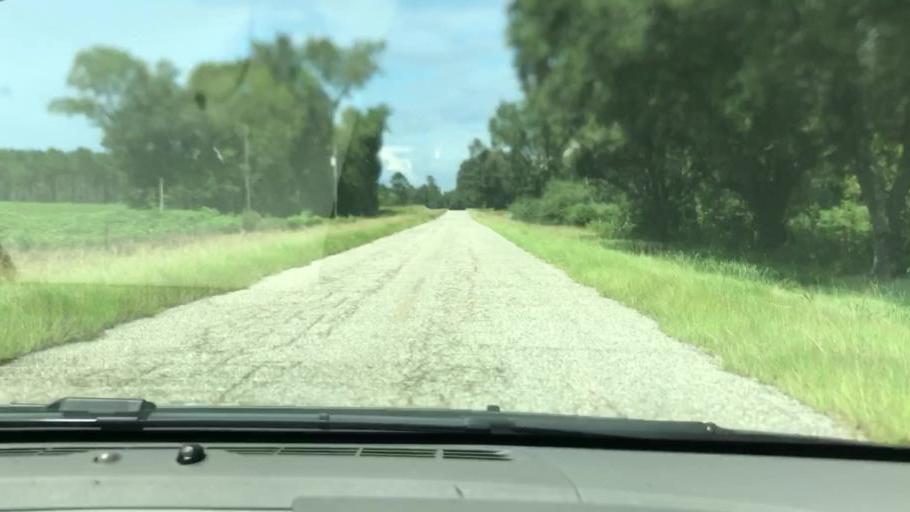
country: US
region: Georgia
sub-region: Early County
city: Blakely
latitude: 31.2165
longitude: -85.0032
